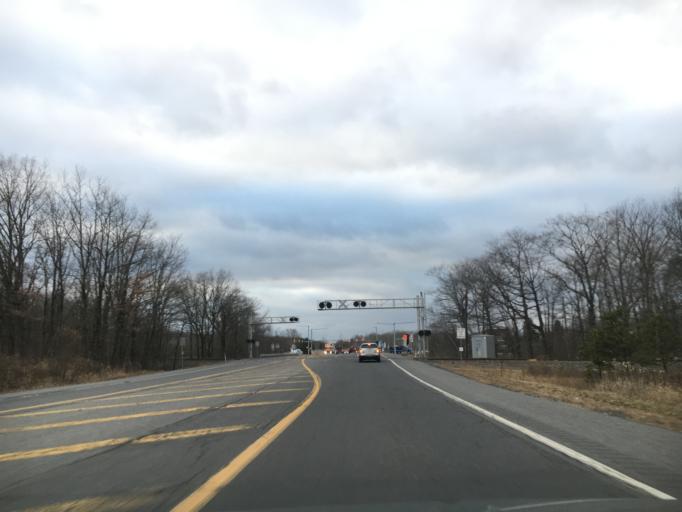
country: US
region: Pennsylvania
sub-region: Schuylkill County
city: McAdoo
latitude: 40.9323
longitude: -75.9911
